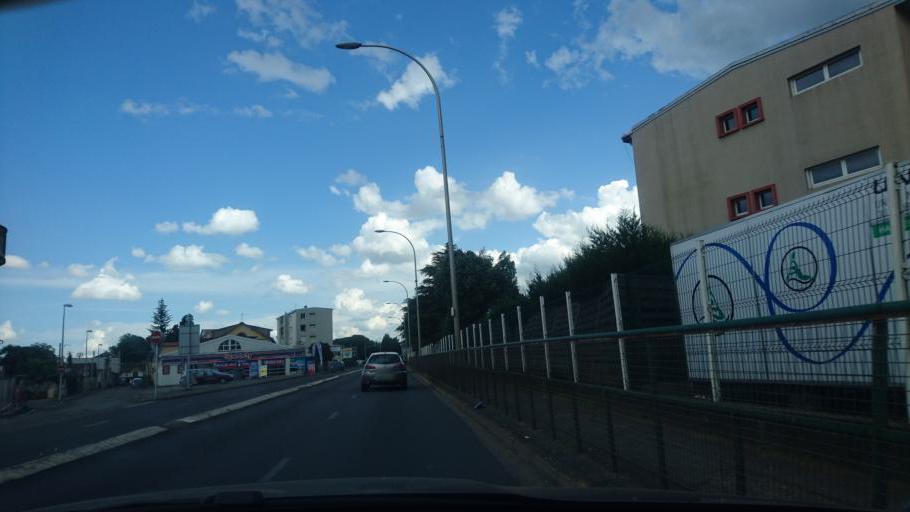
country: FR
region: Midi-Pyrenees
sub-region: Departement des Hautes-Pyrenees
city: Laloubere
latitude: 43.2198
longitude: 0.0671
